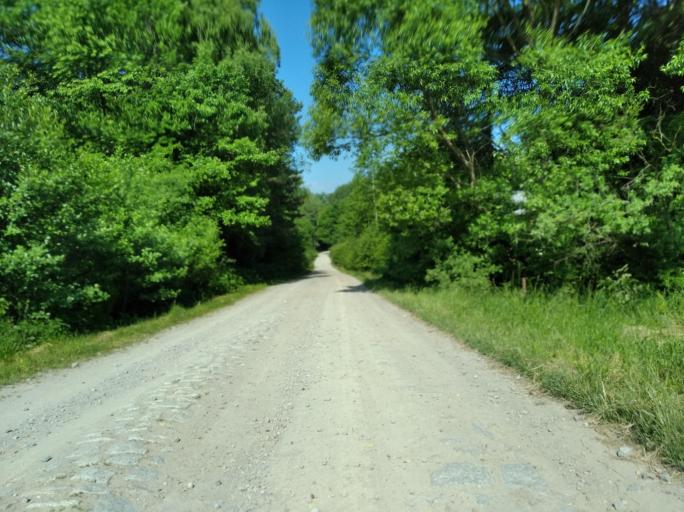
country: PL
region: Subcarpathian Voivodeship
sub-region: Powiat krosnienski
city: Odrzykon
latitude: 49.7694
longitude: 21.7728
